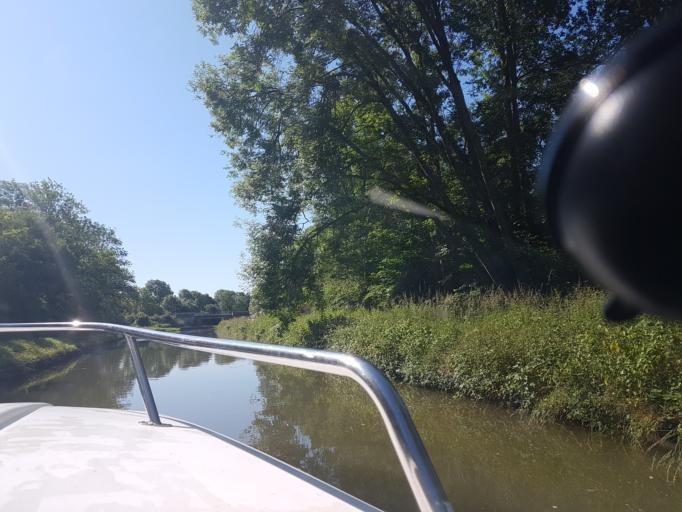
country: FR
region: Bourgogne
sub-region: Departement de la Nievre
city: Clamecy
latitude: 47.5332
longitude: 3.6012
